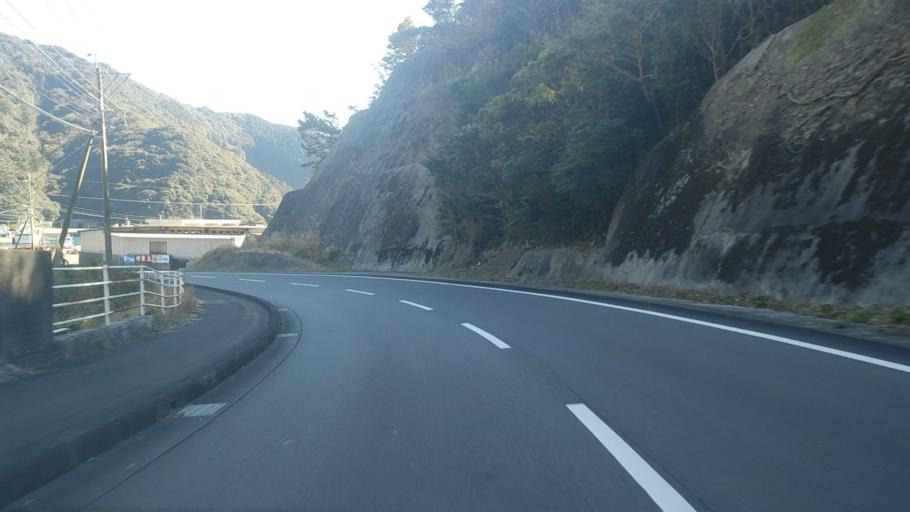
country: JP
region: Oita
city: Saiki
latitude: 32.7934
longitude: 131.9042
